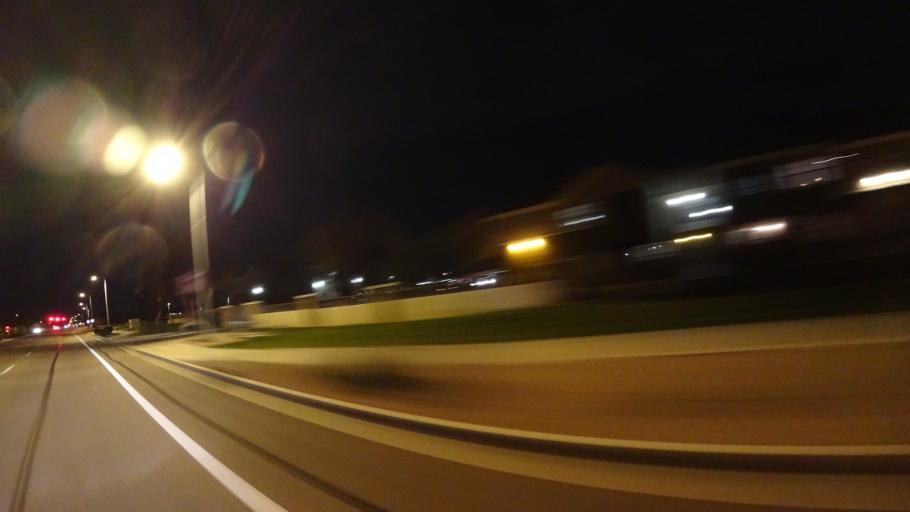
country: US
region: Arizona
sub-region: Maricopa County
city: Chandler
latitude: 33.2914
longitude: -111.8623
